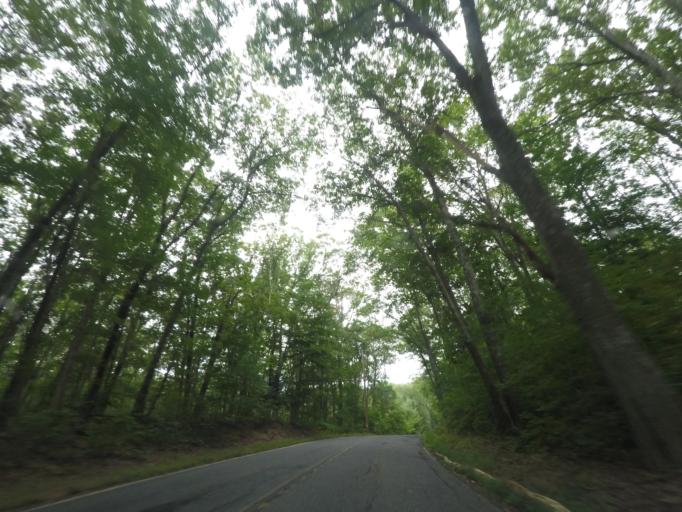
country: US
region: Massachusetts
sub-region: Hampshire County
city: Ware
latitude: 42.2239
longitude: -72.2531
